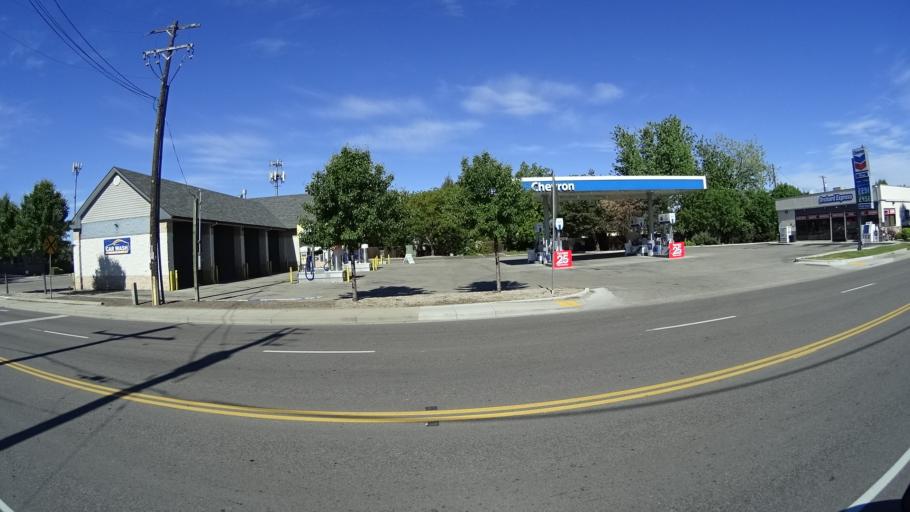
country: US
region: Idaho
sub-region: Ada County
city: Garden City
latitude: 43.6056
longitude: -116.2434
